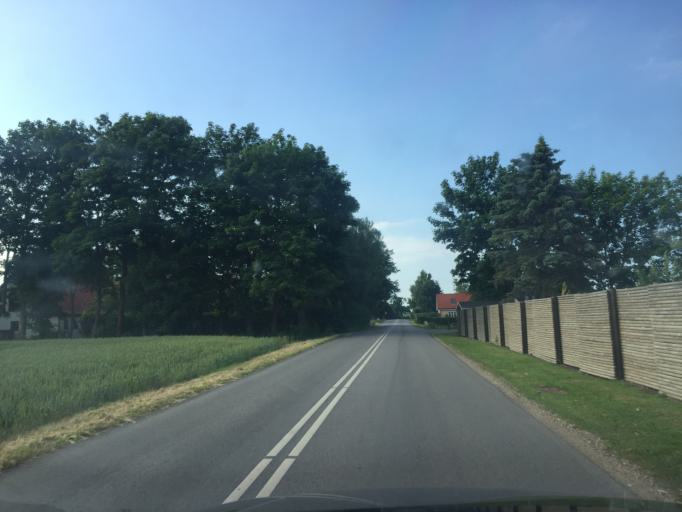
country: DK
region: Capital Region
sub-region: Egedal Kommune
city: Smorumnedre
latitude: 55.7144
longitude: 12.2660
